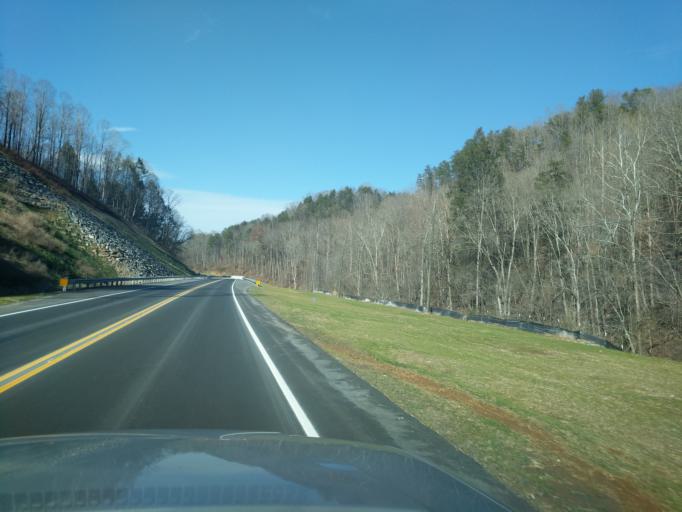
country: US
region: North Carolina
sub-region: McDowell County
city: West Marion
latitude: 35.5733
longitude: -81.9748
